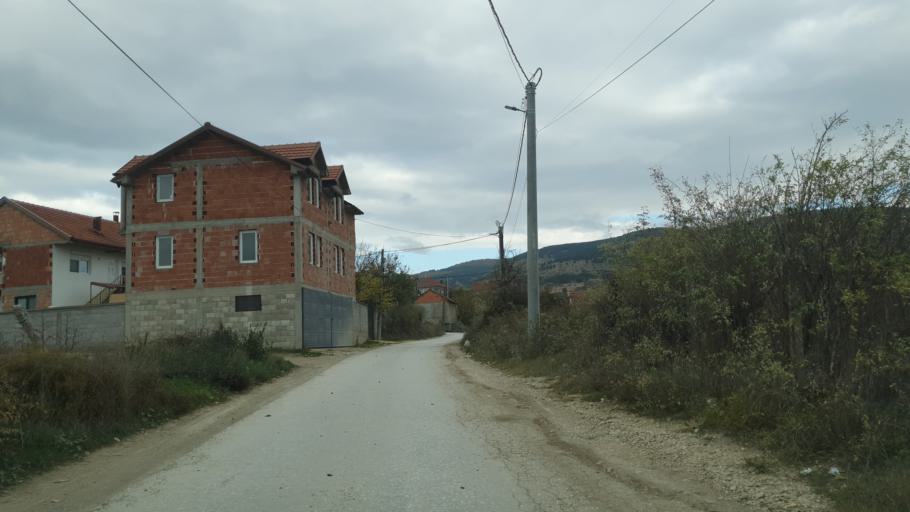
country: MK
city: Kondovo
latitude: 42.0406
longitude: 21.2795
